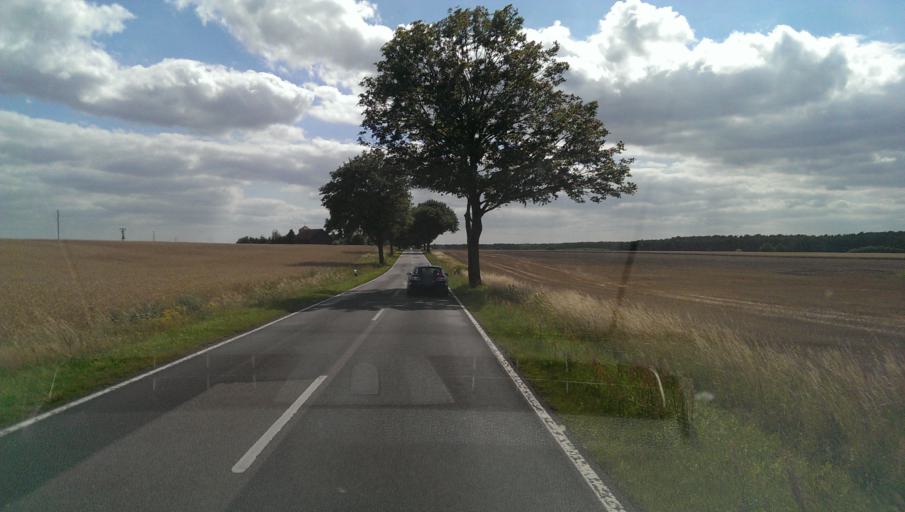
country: DE
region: Saxony-Anhalt
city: Nudersdorf
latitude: 52.0018
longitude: 12.5894
